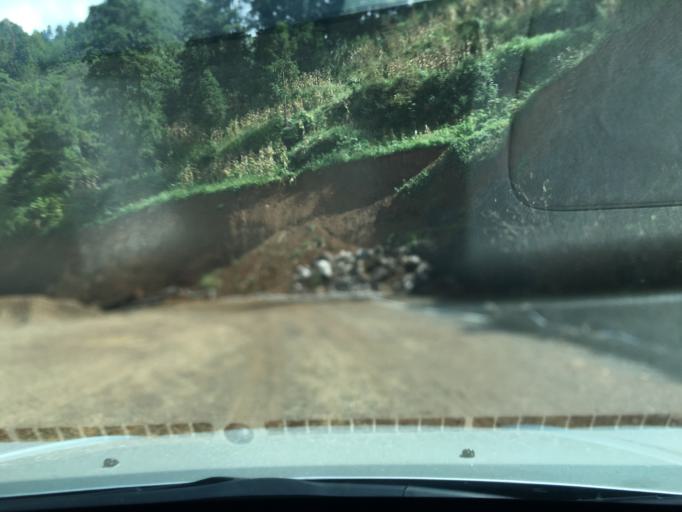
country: CN
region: Guizhou Sheng
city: Liupanshui
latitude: 25.9083
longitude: 105.1067
